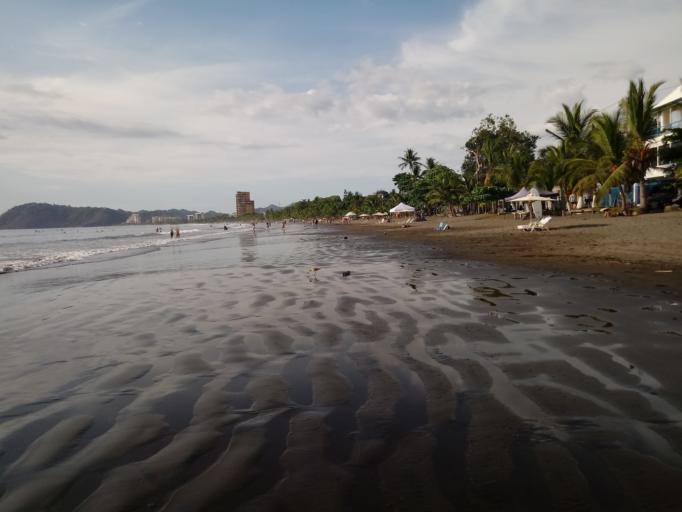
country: CR
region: Puntarenas
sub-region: Canton de Garabito
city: Jaco
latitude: 9.6007
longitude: -84.6207
